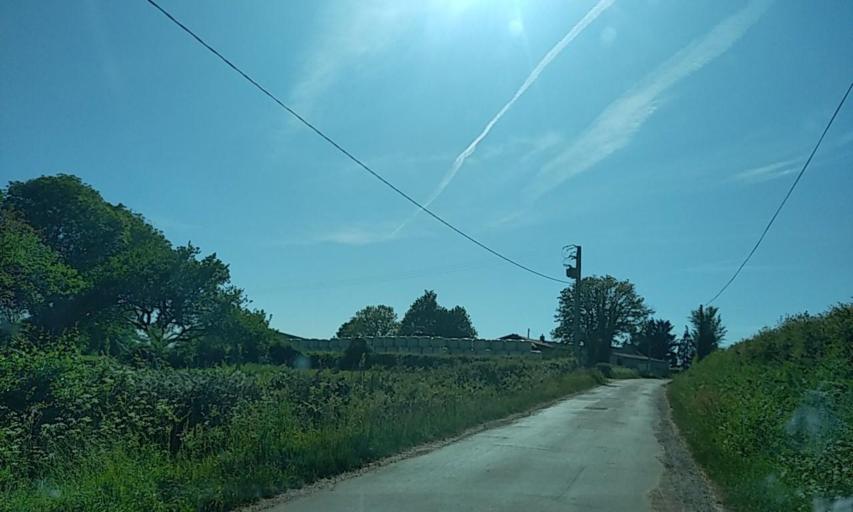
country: FR
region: Poitou-Charentes
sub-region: Departement des Deux-Sevres
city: Boisme
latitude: 46.7773
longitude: -0.4075
